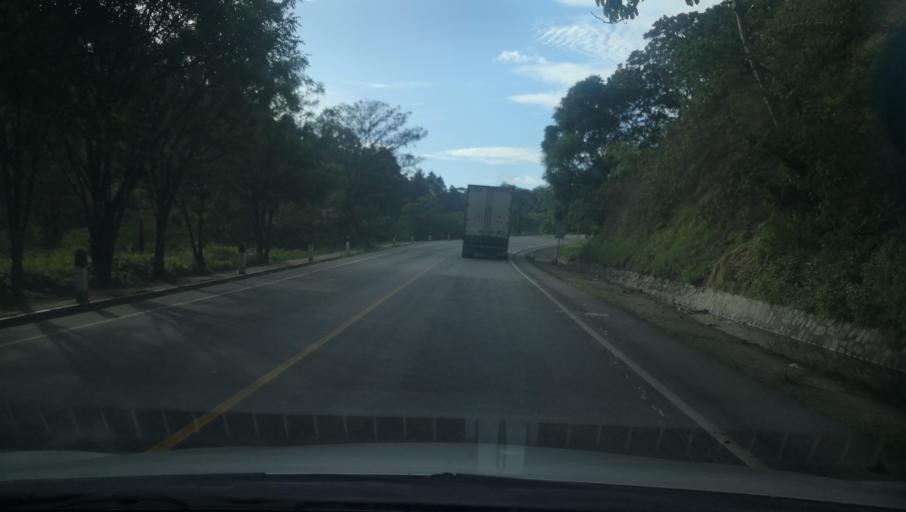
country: NI
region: Nueva Segovia
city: Mozonte
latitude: 13.7235
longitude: -86.5069
